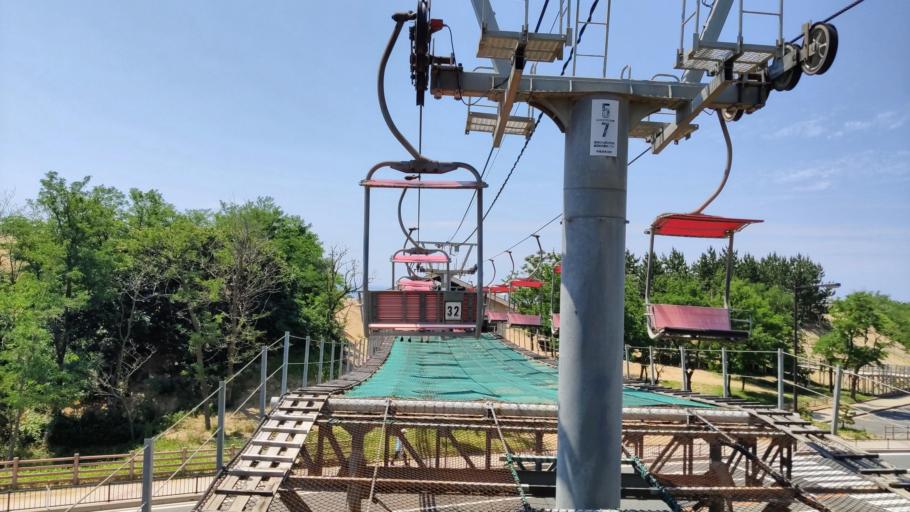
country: JP
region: Tottori
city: Tottori
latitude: 35.5420
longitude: 134.2374
